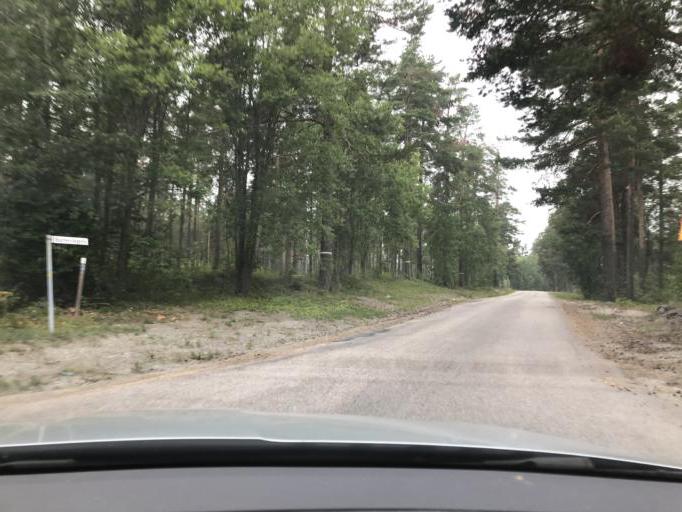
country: SE
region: Vaesternorrland
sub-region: Sundsvalls Kommun
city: Sundsvall
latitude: 62.4006
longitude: 17.3098
